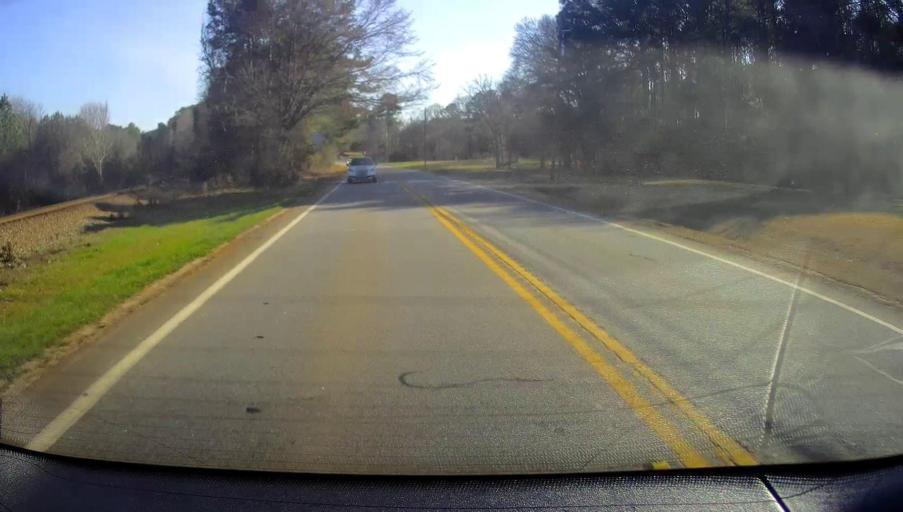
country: US
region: Georgia
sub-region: Butts County
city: Indian Springs
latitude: 33.2738
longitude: -83.9162
